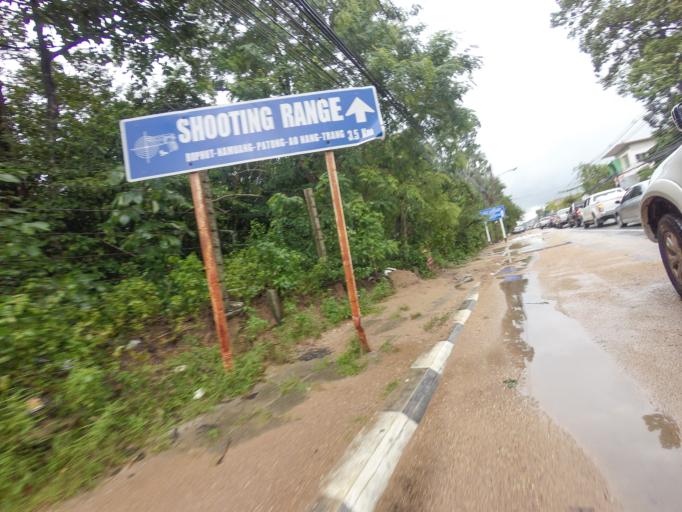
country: TH
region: Surat Thani
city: Ko Samui
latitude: 9.5155
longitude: 100.0501
